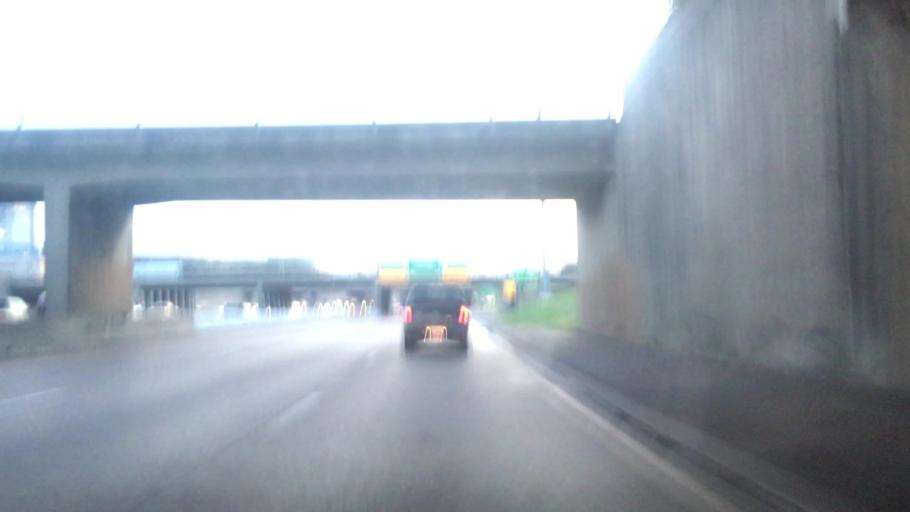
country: US
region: Texas
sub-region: Dallas County
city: Dallas
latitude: 32.7703
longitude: -96.8013
